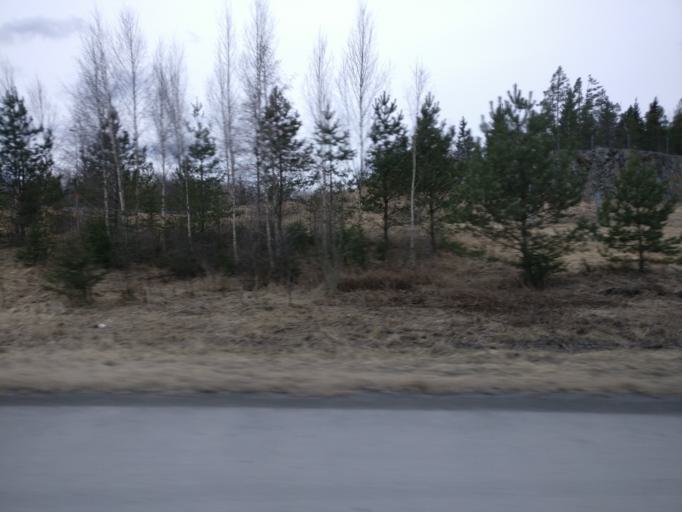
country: FI
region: Pirkanmaa
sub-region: Etelae-Pirkanmaa
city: Akaa
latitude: 61.1629
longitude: 23.9581
